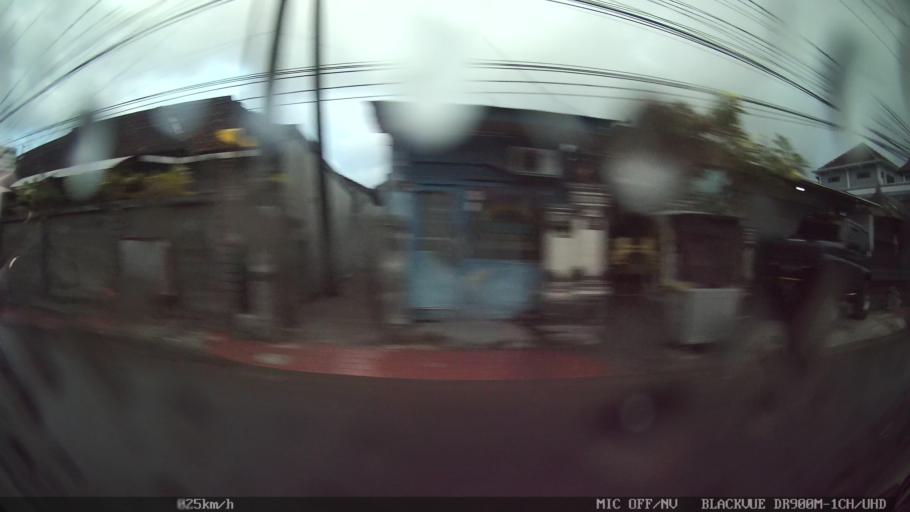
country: ID
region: Bali
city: Banjar Kayangan
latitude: -8.6264
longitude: 115.2240
